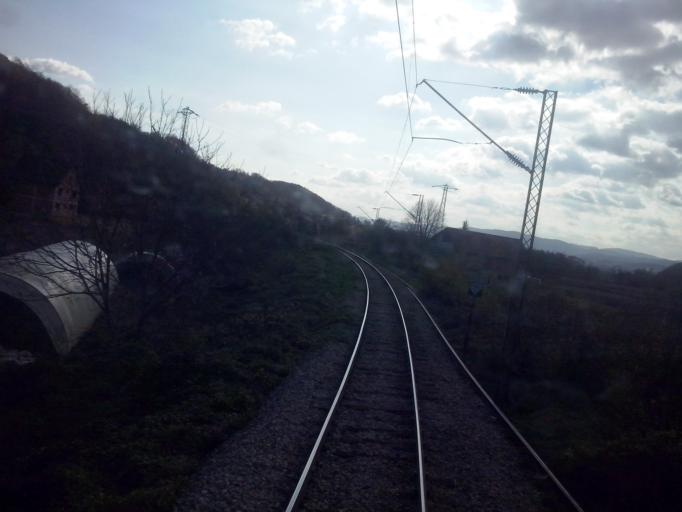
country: RS
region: Central Serbia
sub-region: Zlatiborski Okrug
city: Pozega
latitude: 43.8925
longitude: 19.9960
